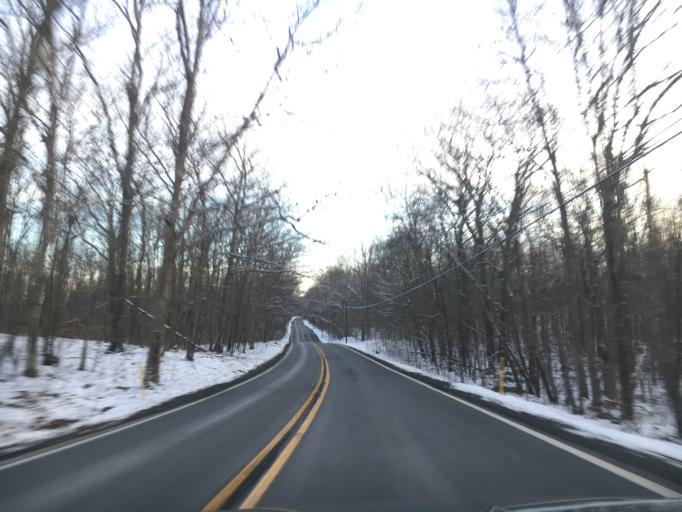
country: US
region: Pennsylvania
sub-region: Pike County
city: Saw Creek
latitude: 41.1559
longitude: -75.0821
